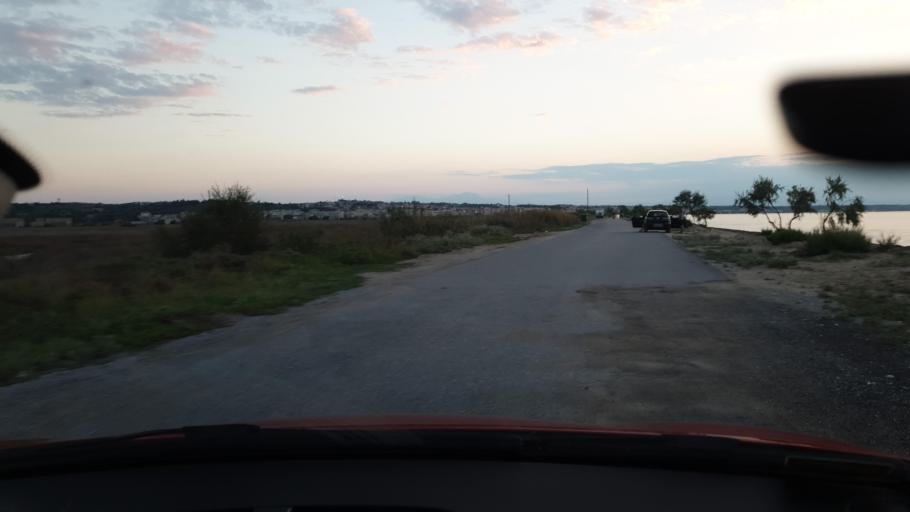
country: GR
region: Central Macedonia
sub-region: Nomos Thessalonikis
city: Peraia
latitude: 40.5176
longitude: 22.9465
